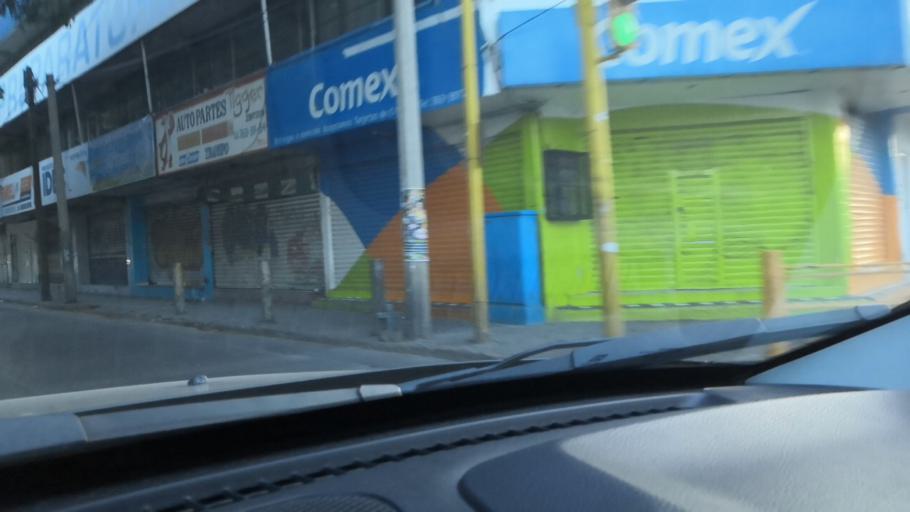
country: MX
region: Guanajuato
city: Leon
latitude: 21.1279
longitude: -101.6607
